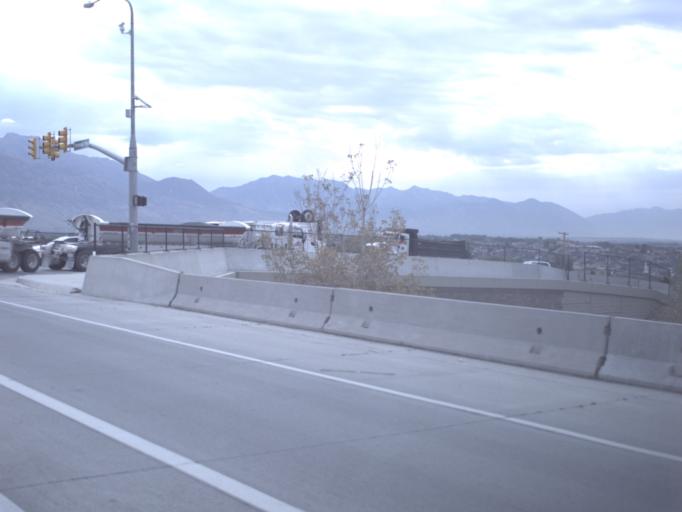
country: US
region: Utah
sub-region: Utah County
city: Lehi
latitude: 40.4326
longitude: -111.8695
